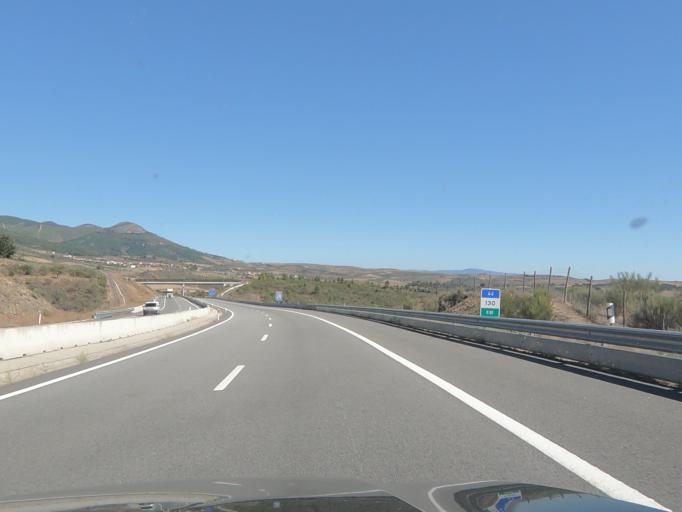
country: PT
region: Vila Real
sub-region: Murca
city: Murca
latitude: 41.4207
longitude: -7.3733
